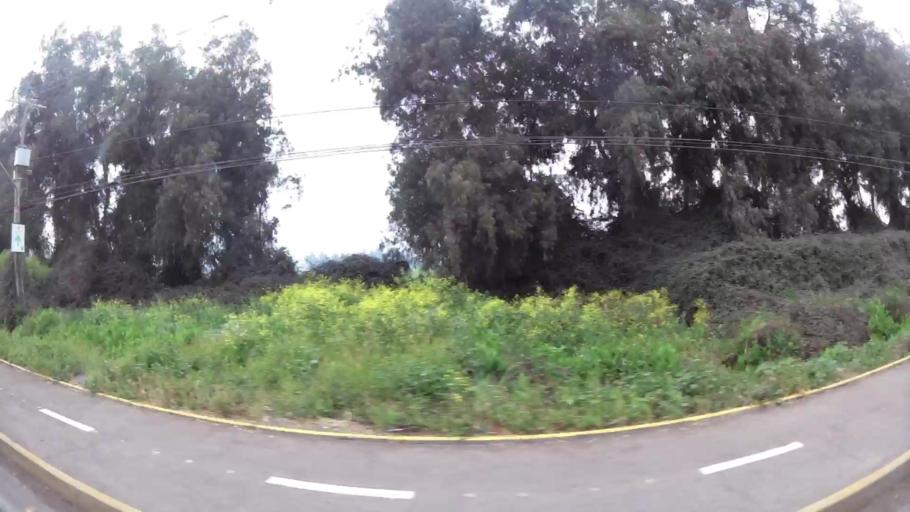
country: CL
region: Santiago Metropolitan
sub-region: Provincia de Chacabuco
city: Lampa
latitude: -33.2367
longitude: -70.7689
